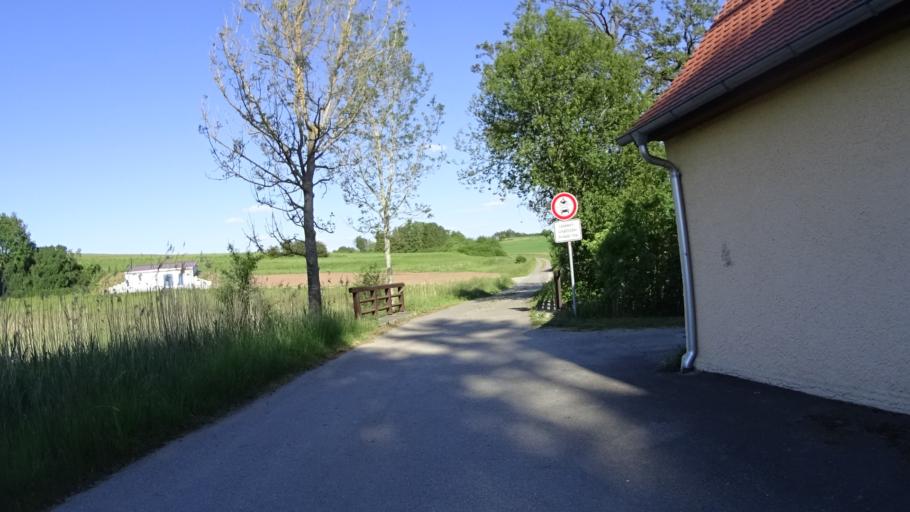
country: DE
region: Bavaria
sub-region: Regierungsbezirk Mittelfranken
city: Feuchtwangen
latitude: 49.1627
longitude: 10.3581
